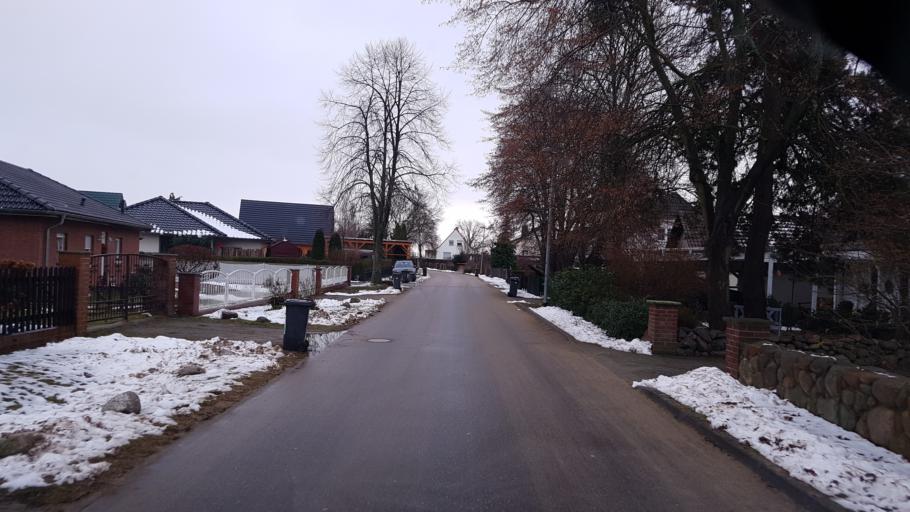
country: DE
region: Brandenburg
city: Luebben
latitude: 51.9389
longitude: 13.9157
